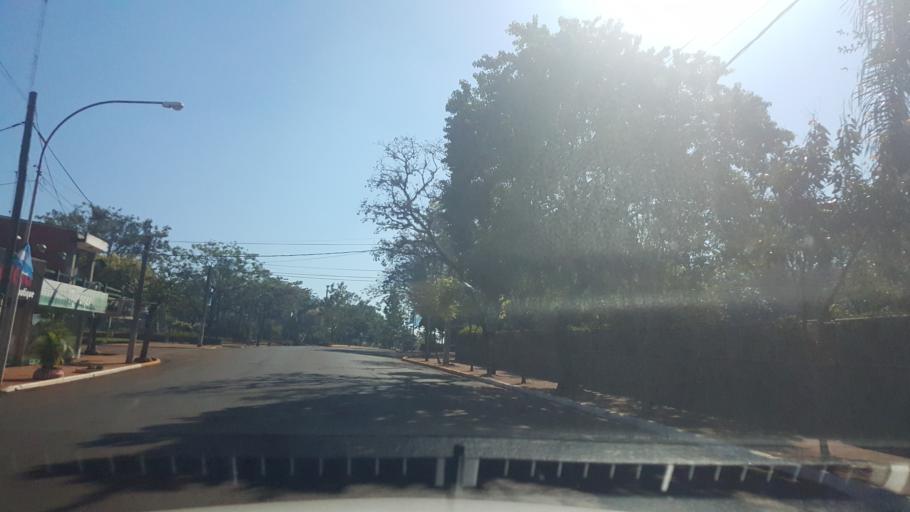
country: AR
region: Misiones
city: Puerto Rico
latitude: -26.8184
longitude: -55.0269
